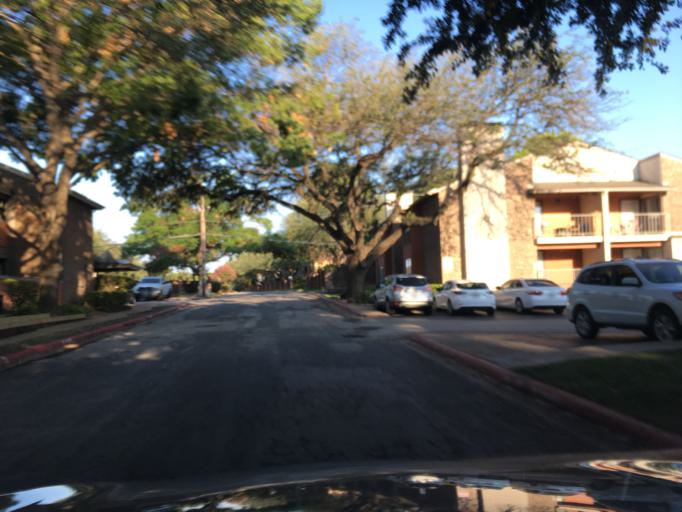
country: US
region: Texas
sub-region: Dallas County
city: Addison
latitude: 32.9653
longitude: -96.8149
